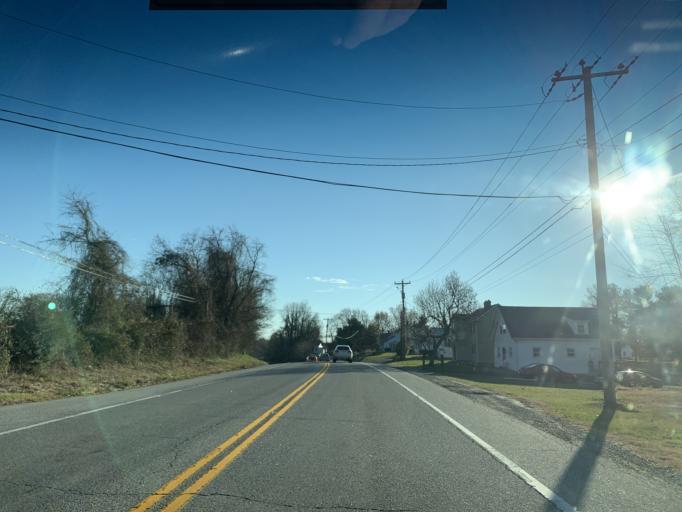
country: US
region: Delaware
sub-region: New Castle County
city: Middletown
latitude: 39.3685
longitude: -75.8835
